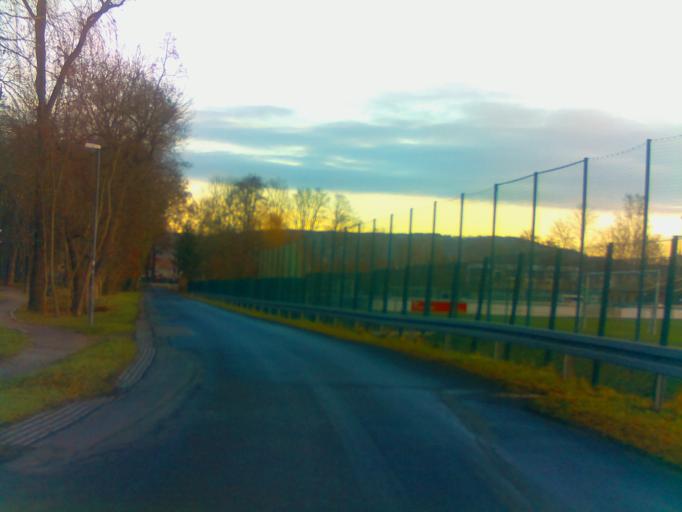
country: DE
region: Thuringia
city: Bad Blankenburg
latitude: 50.6748
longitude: 11.2706
